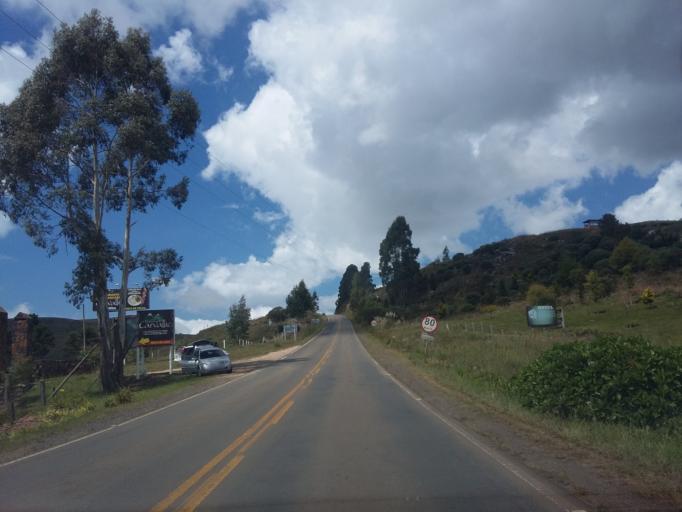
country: BR
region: Santa Catarina
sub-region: Lauro Muller
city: Lauro Muller
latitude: -28.3493
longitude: -49.5985
